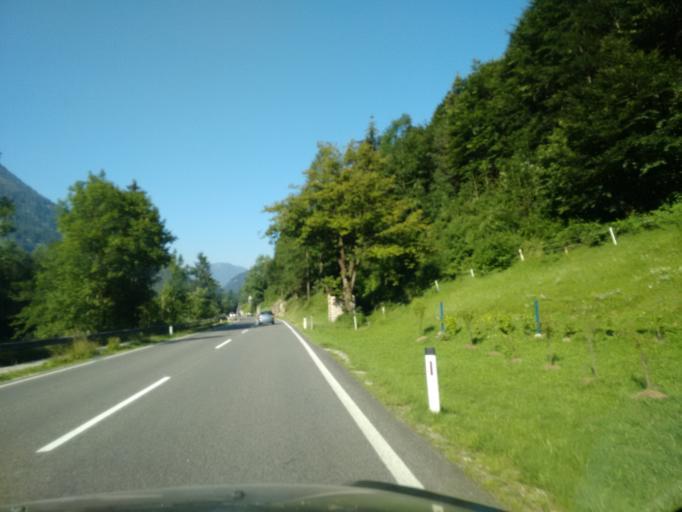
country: AT
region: Upper Austria
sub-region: Politischer Bezirk Gmunden
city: Bad Ischl
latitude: 47.7540
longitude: 13.6983
